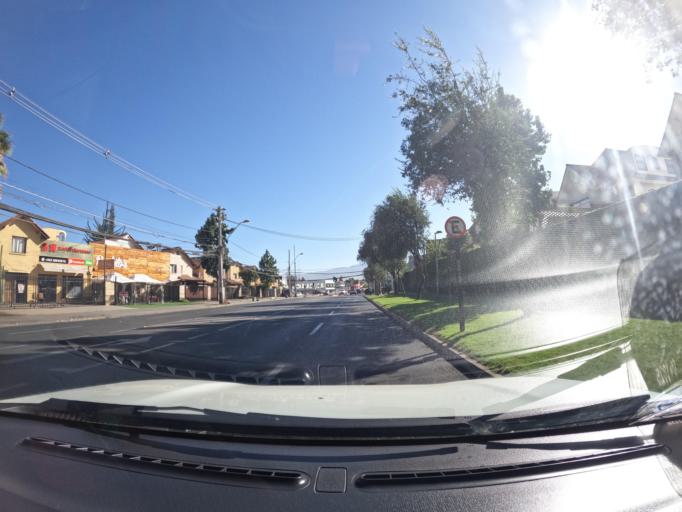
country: CL
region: Santiago Metropolitan
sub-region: Provincia de Santiago
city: Villa Presidente Frei, Nunoa, Santiago, Chile
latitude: -33.4801
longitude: -70.5452
